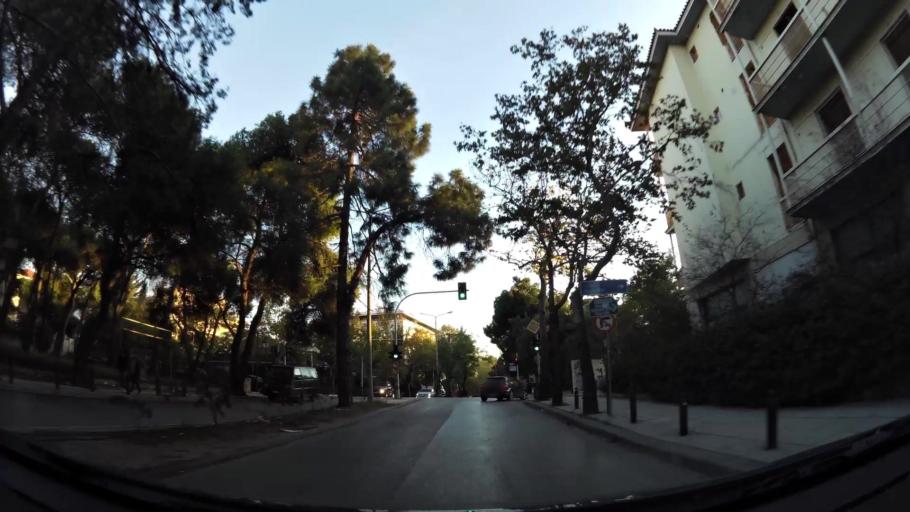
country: GR
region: Attica
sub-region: Nomarchia Athinas
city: Kifisia
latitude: 38.0755
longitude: 23.8210
